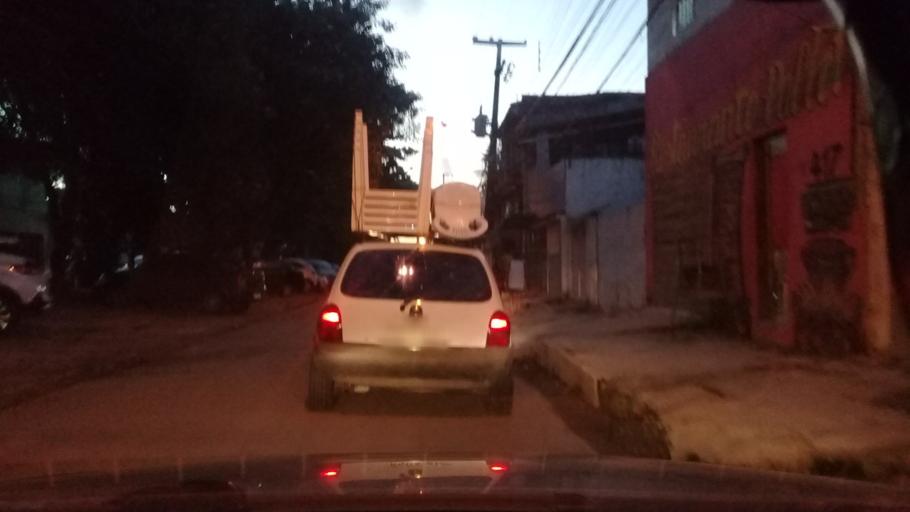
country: BR
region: Pernambuco
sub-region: Recife
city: Recife
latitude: -8.1143
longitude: -34.9171
